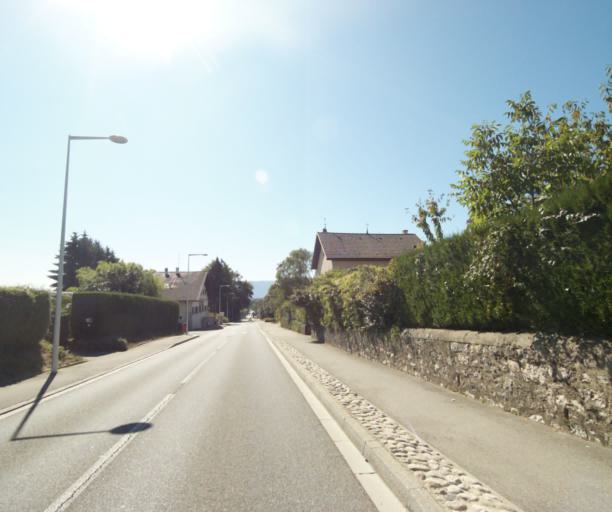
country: FR
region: Rhone-Alpes
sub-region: Departement de l'Ain
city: Ornex
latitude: 46.2676
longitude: 6.0999
